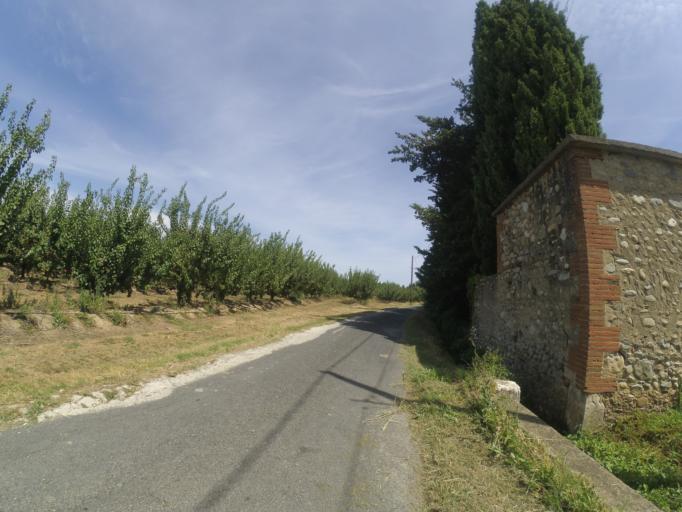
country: FR
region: Languedoc-Roussillon
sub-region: Departement des Pyrenees-Orientales
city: Millas
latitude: 42.6830
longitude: 2.6711
